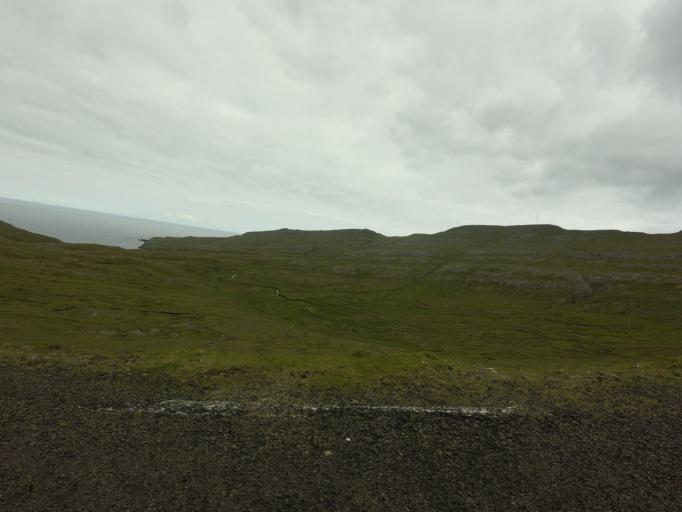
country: FO
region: Suduroy
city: Vagur
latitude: 61.4360
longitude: -6.7554
